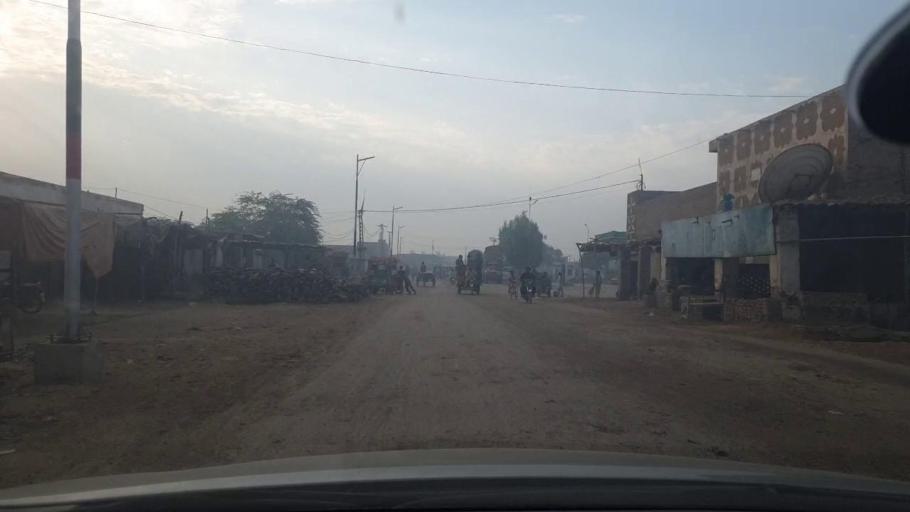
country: PK
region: Sindh
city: Jacobabad
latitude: 28.2835
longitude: 68.4240
